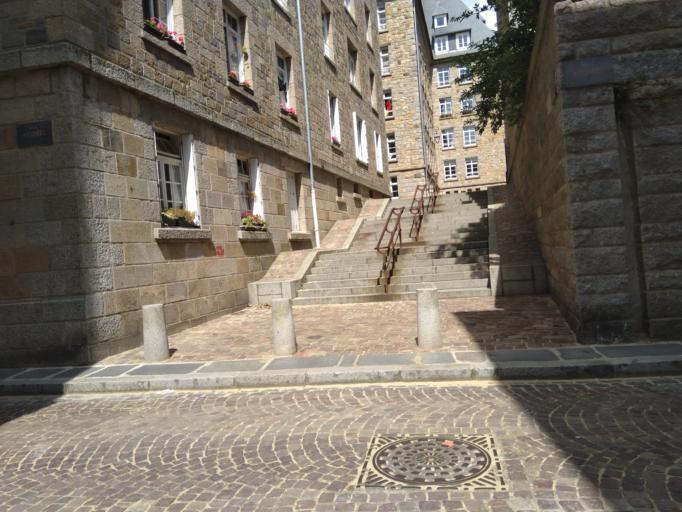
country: FR
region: Brittany
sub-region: Departement d'Ille-et-Vilaine
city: Saint-Malo
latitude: 48.6468
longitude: -2.0277
